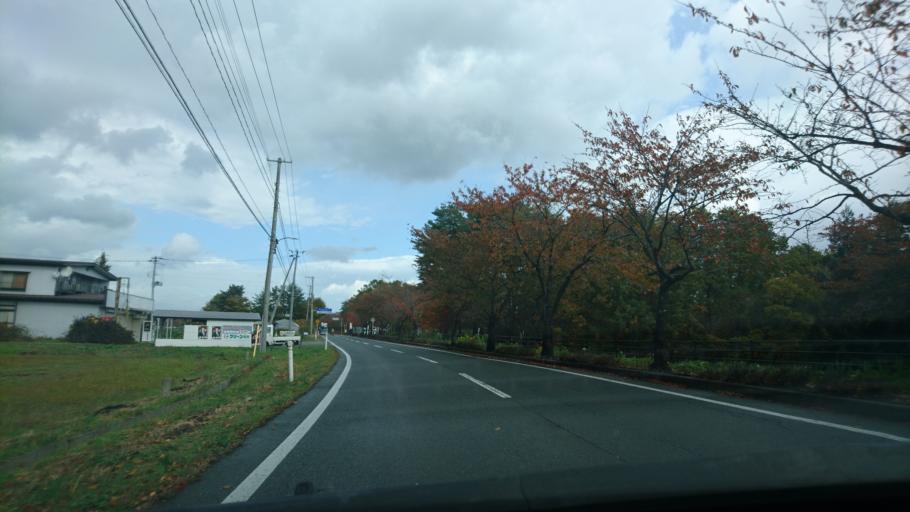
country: JP
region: Iwate
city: Shizukuishi
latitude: 39.6859
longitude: 141.0216
